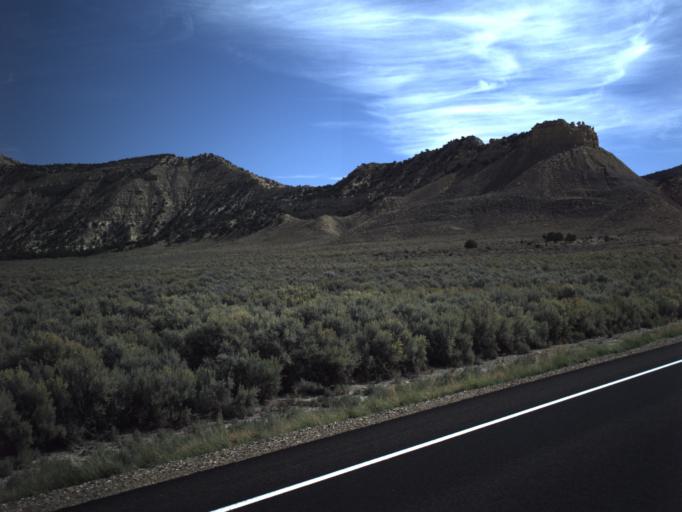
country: US
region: Utah
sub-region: Garfield County
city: Panguitch
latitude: 37.5974
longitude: -111.9489
